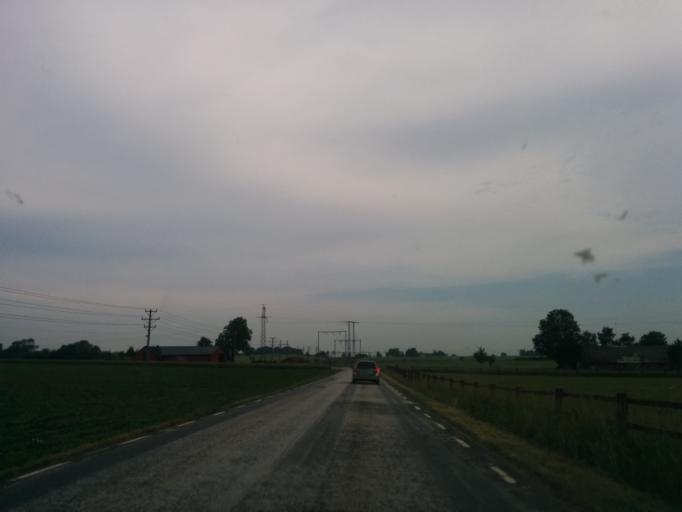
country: SE
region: Skane
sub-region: Lunds Kommun
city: Genarp
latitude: 55.6337
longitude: 13.3739
